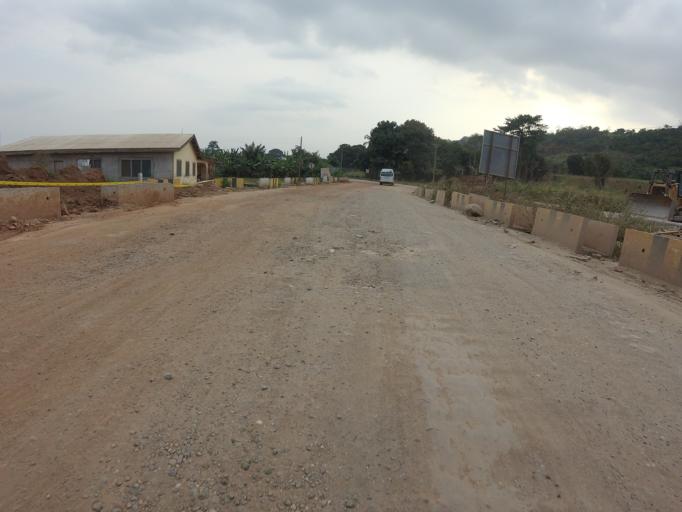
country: GH
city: Akropong
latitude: 6.3099
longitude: 0.1510
